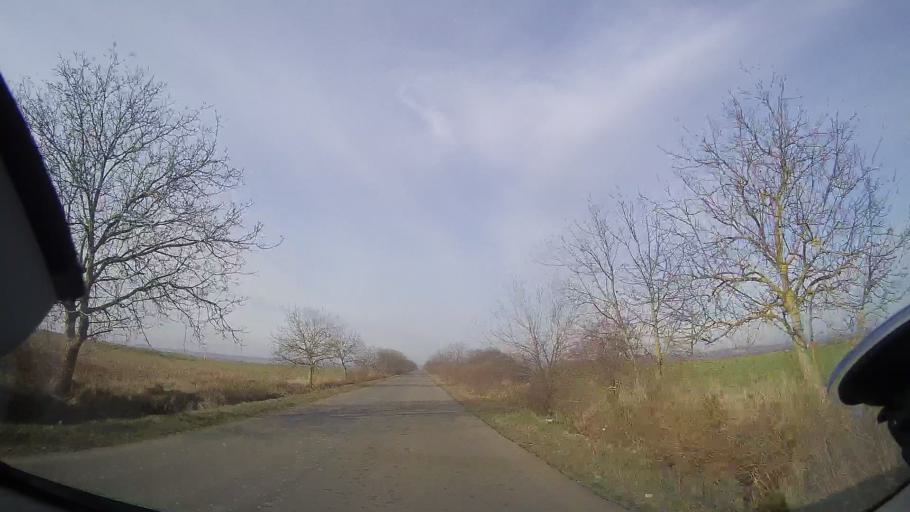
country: RO
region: Bihor
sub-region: Comuna Spinus
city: Spinus
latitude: 47.2167
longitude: 22.1748
